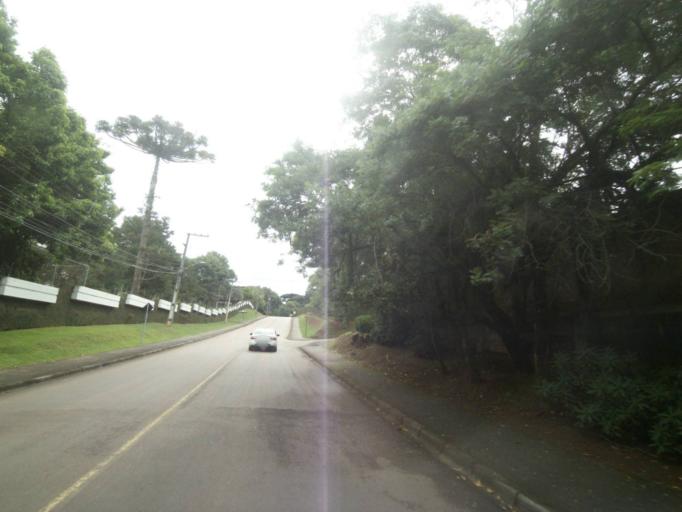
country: BR
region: Parana
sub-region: Curitiba
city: Curitiba
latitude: -25.4530
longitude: -49.3304
